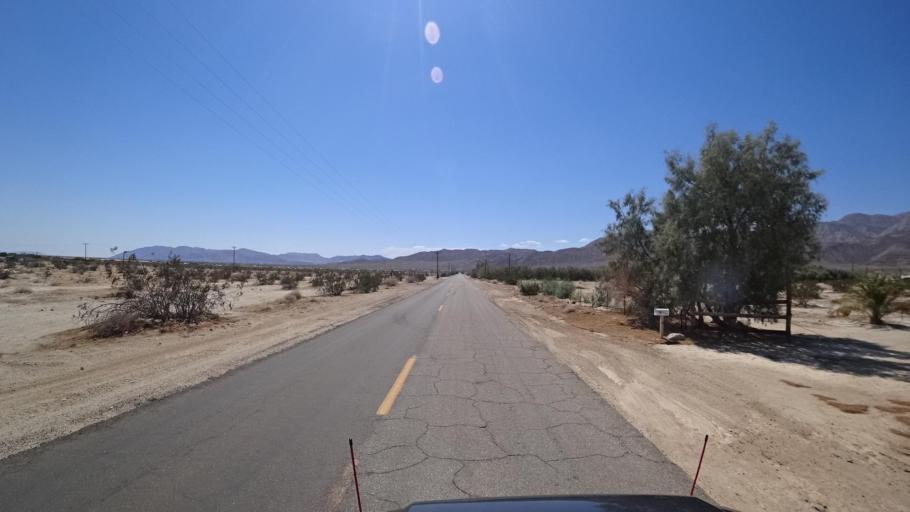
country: US
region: California
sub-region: Imperial County
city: Salton City
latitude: 33.1125
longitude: -116.1328
